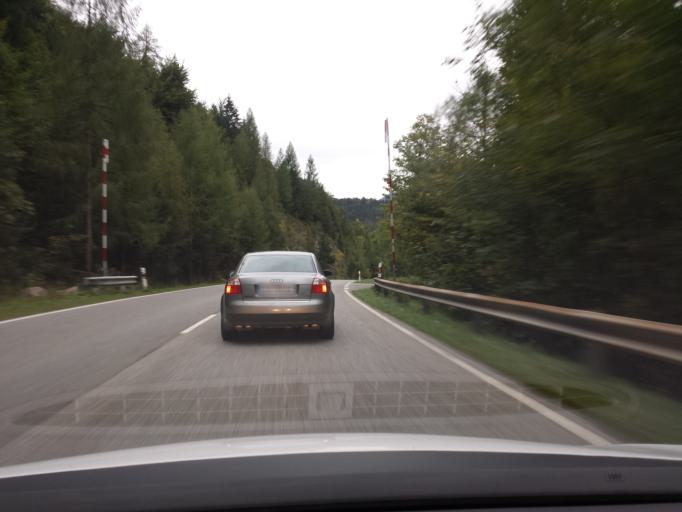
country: DE
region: Bavaria
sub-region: Upper Bavaria
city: Schneizlreuth
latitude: 47.6807
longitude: 12.8342
